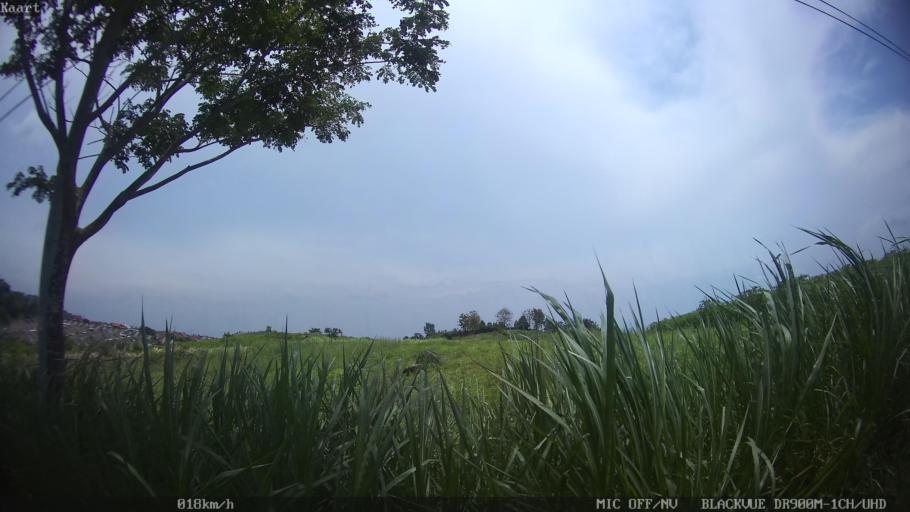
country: ID
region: Lampung
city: Bandarlampung
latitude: -5.4115
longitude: 105.2039
